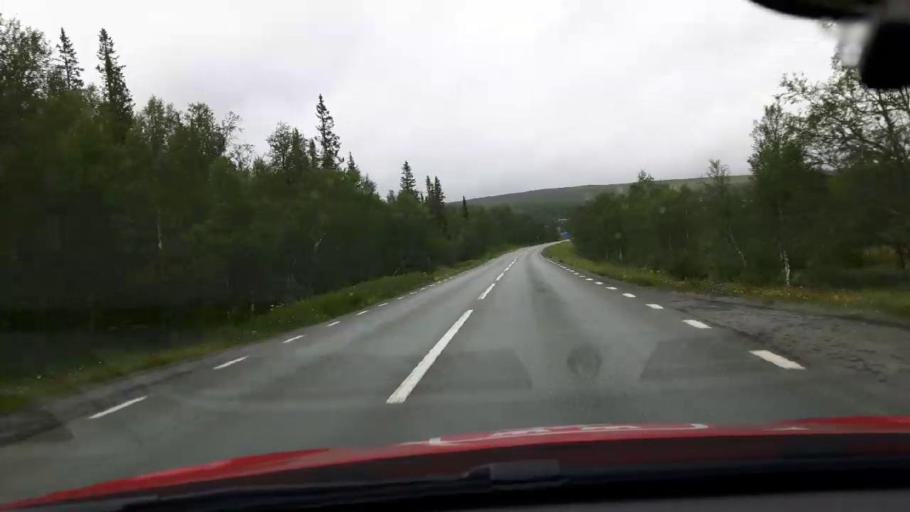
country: NO
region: Nord-Trondelag
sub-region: Meraker
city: Meraker
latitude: 63.3051
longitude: 12.1093
